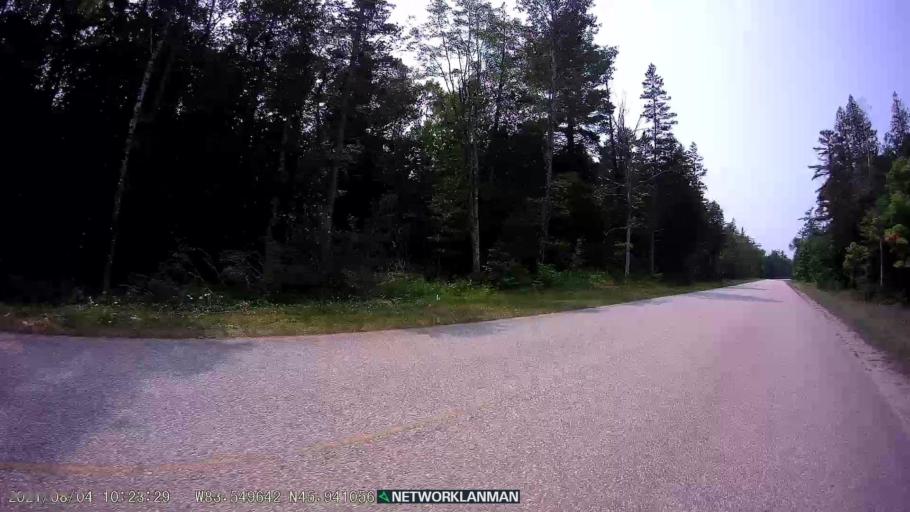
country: CA
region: Ontario
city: Thessalon
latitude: 45.9410
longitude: -83.5506
